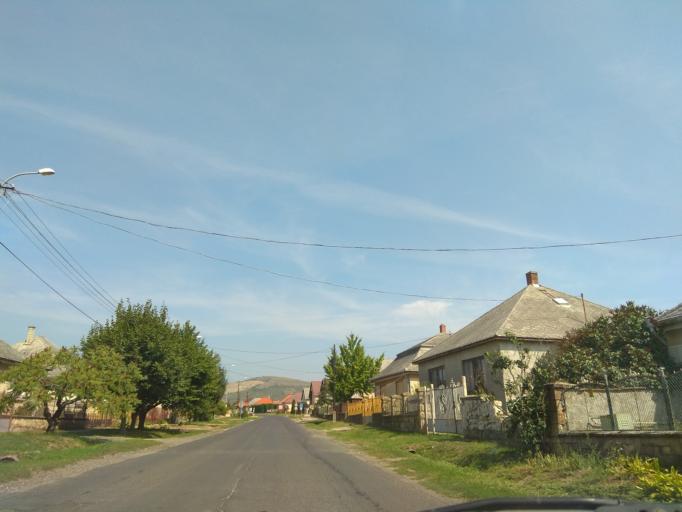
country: HU
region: Borsod-Abauj-Zemplen
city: Tallya
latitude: 48.2193
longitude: 21.2255
